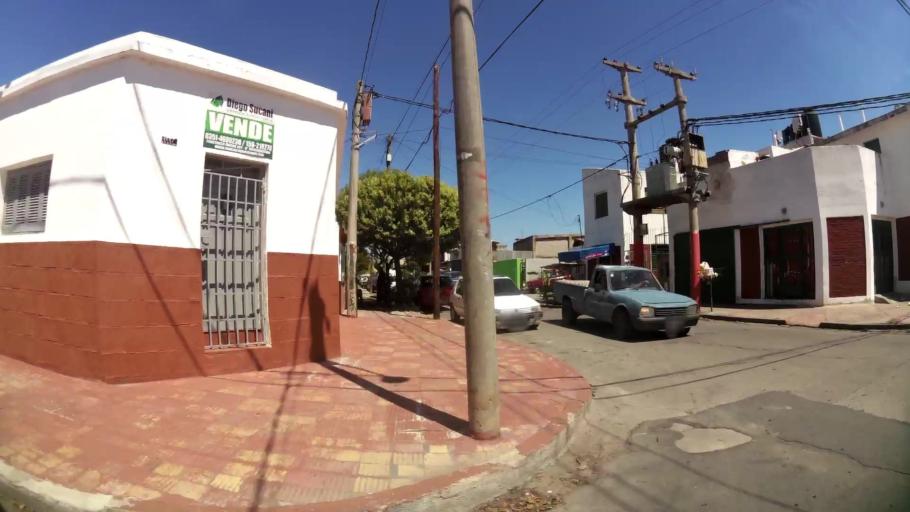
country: AR
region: Cordoba
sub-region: Departamento de Capital
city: Cordoba
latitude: -31.4257
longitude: -64.2077
